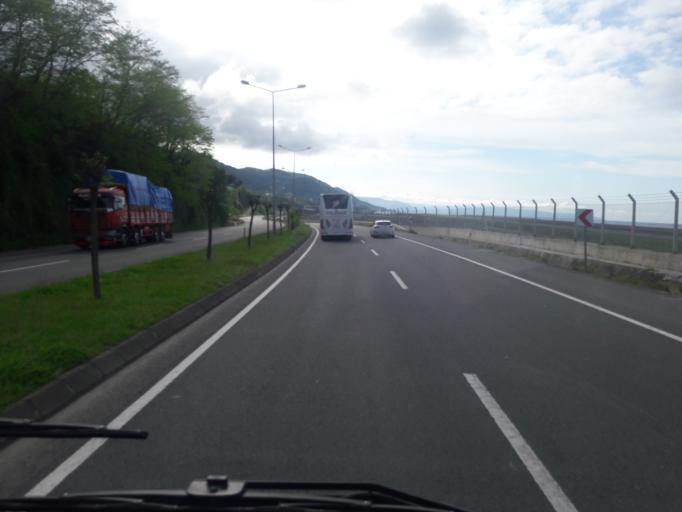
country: TR
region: Giresun
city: Piraziz
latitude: 40.9626
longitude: 38.0960
